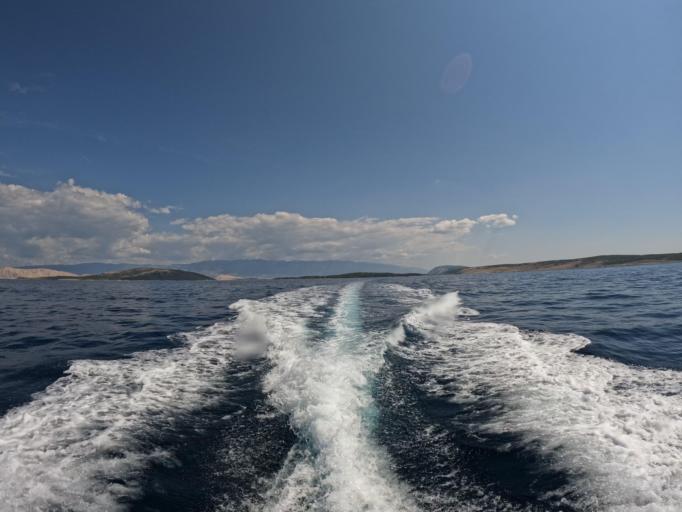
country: HR
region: Primorsko-Goranska
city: Lopar
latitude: 44.8638
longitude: 14.6889
